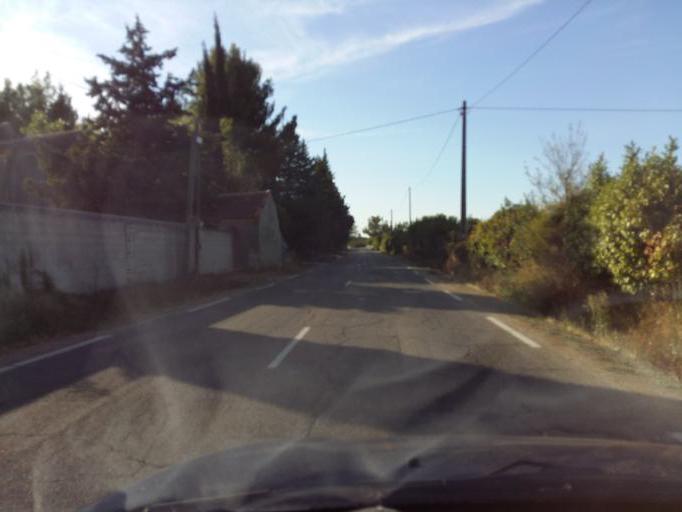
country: FR
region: Provence-Alpes-Cote d'Azur
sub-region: Departement du Vaucluse
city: Carpentras
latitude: 44.0407
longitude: 5.0647
